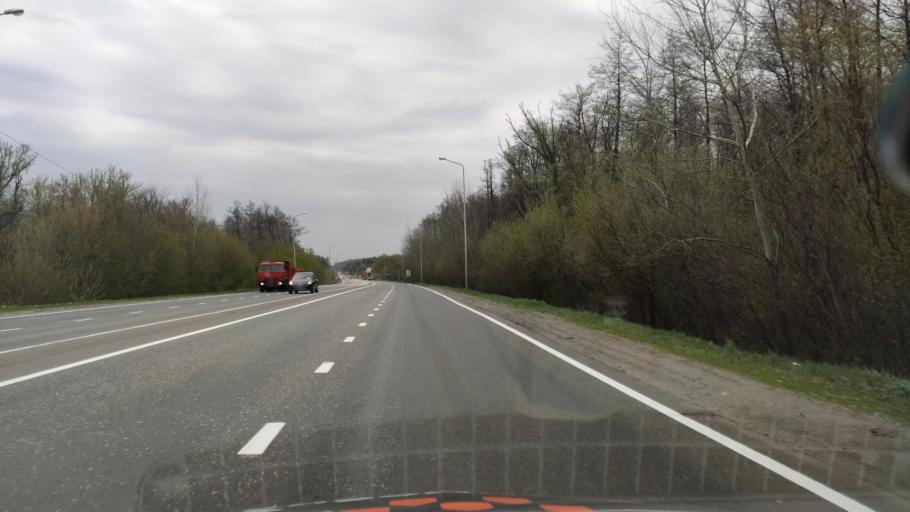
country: RU
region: Belgorod
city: Staryy Oskol
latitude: 51.3503
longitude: 37.8273
